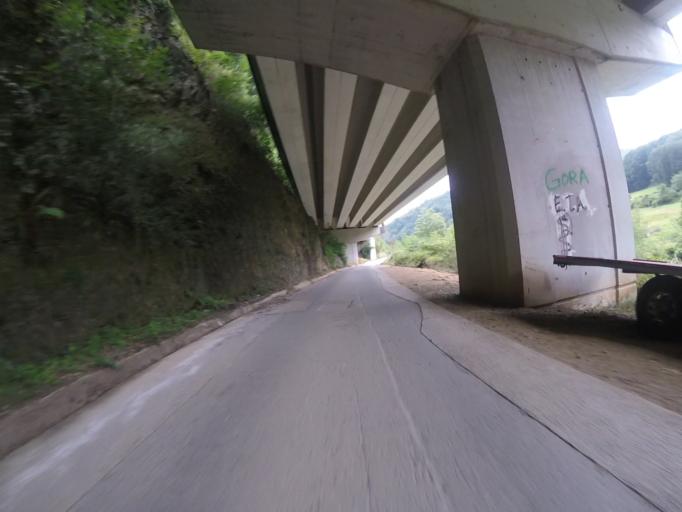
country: ES
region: Navarre
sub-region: Provincia de Navarra
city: Sunbilla
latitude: 43.1807
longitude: -1.6709
